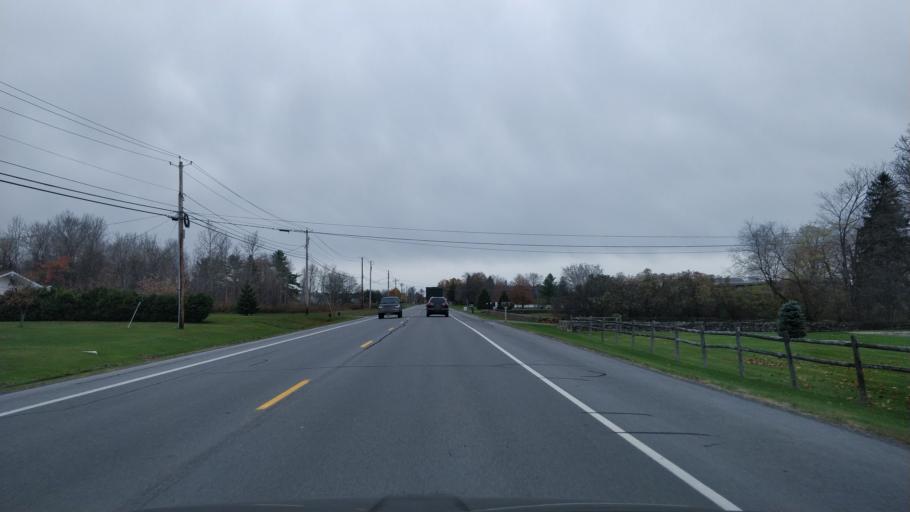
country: CA
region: Ontario
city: Prescott
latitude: 44.6650
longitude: -75.5388
